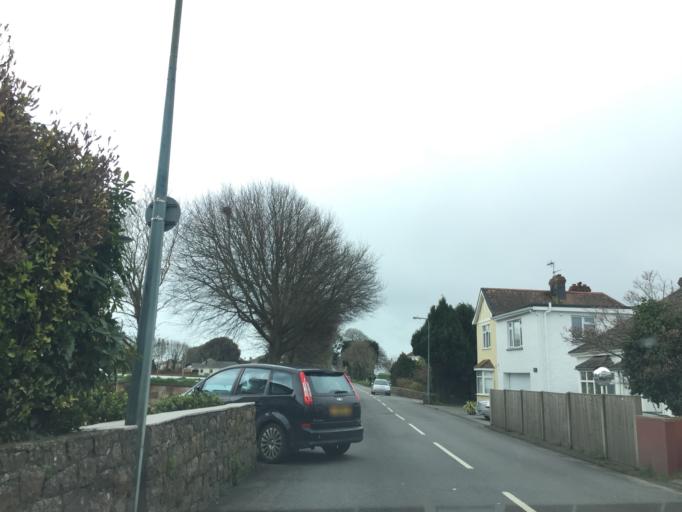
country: JE
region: St Helier
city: Saint Helier
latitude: 49.2086
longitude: -2.1426
